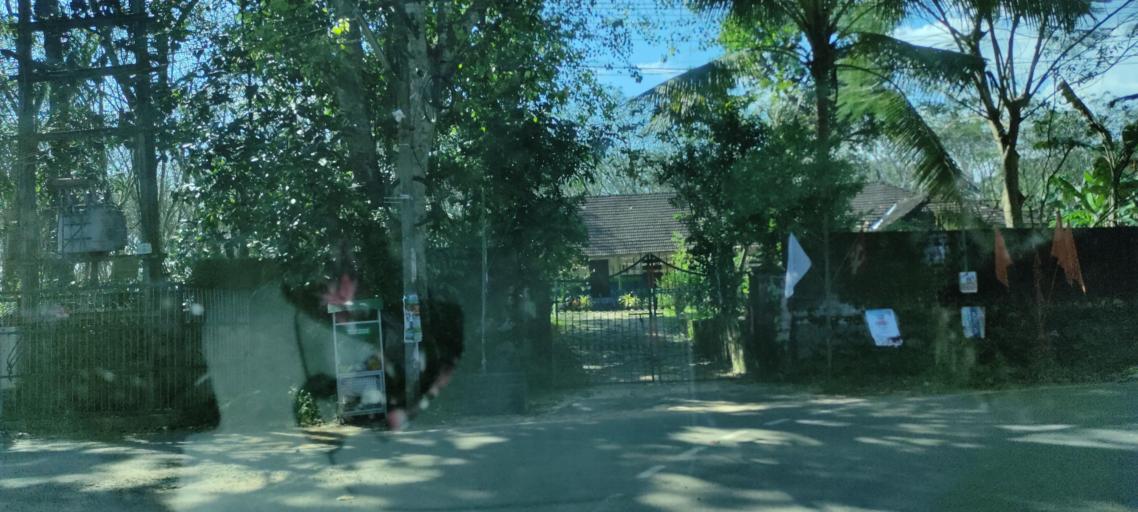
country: IN
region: Kerala
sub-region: Pattanamtitta
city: Adur
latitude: 9.2000
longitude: 76.7522
